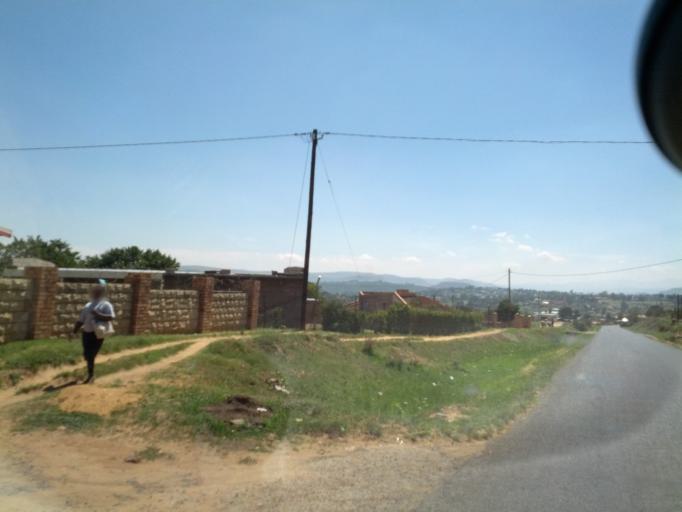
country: LS
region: Butha-Buthe
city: Butha-Buthe
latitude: -28.7778
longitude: 28.2318
